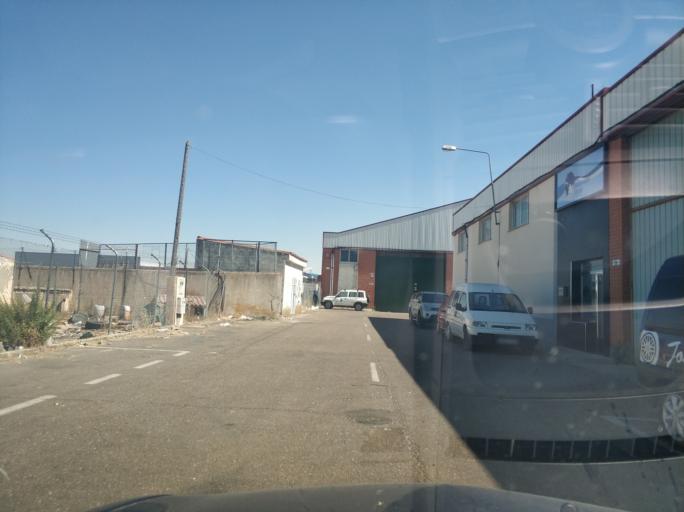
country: ES
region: Castille and Leon
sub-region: Provincia de Salamanca
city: Villares de la Reina
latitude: 40.9938
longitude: -5.6400
